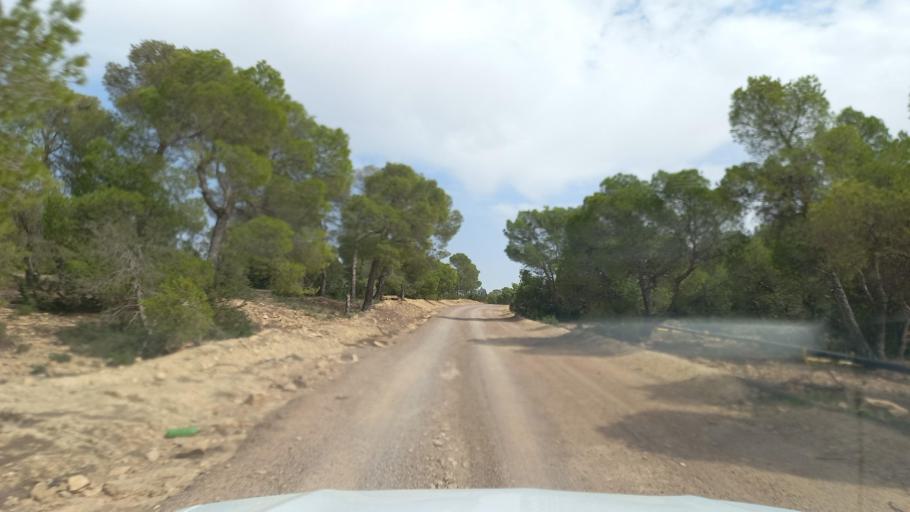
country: TN
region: Al Qasrayn
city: Kasserine
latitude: 35.3821
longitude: 8.8903
